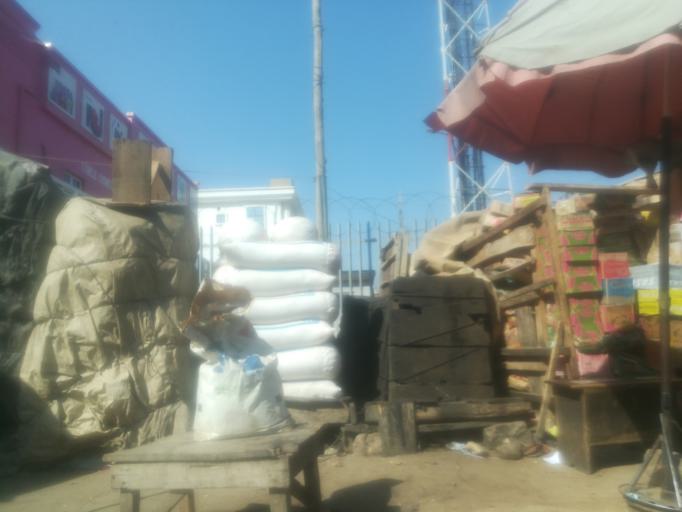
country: NG
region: Kano
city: Kano
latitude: 12.0104
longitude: 8.5352
